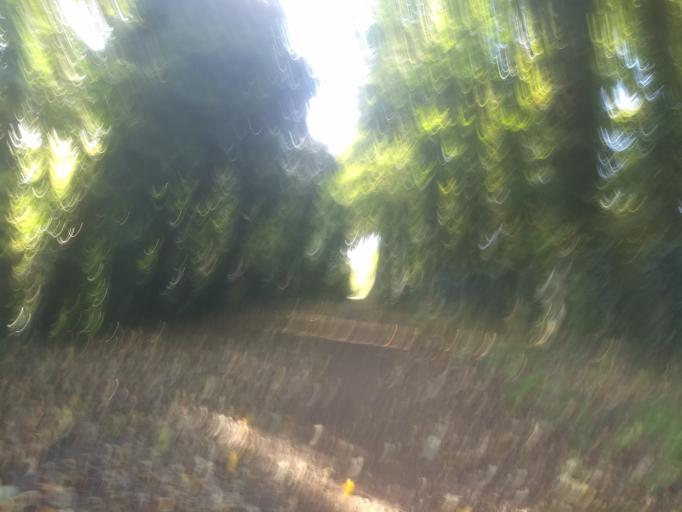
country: FR
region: Nord-Pas-de-Calais
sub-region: Departement du Pas-de-Calais
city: Saint-Laurent-Blangy
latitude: 50.3029
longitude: 2.8161
